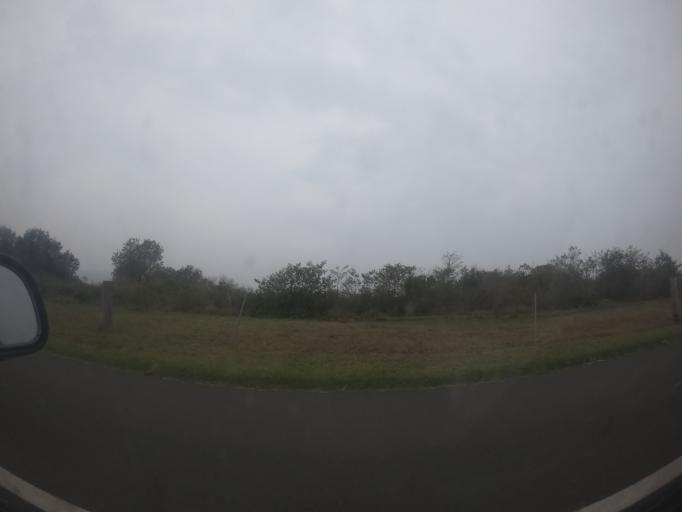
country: AU
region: New South Wales
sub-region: Shellharbour
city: Croom
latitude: -34.6122
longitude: 150.8564
